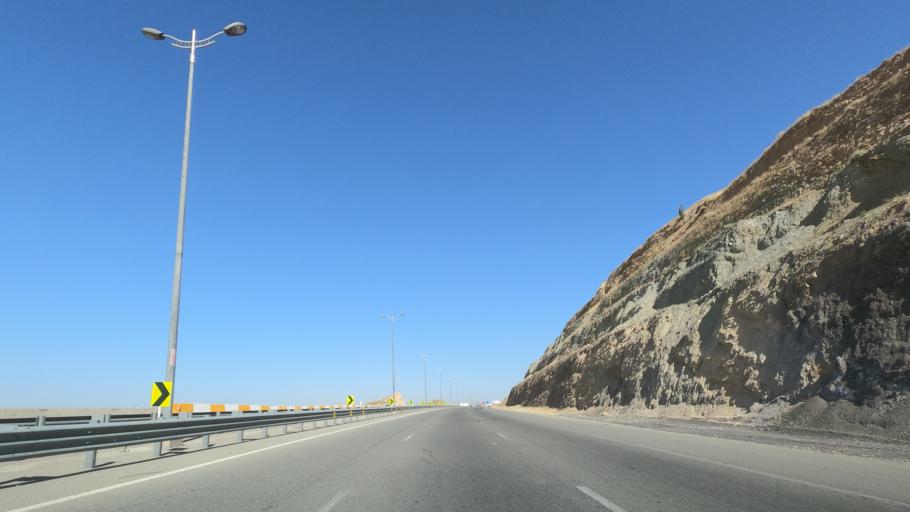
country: IR
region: Tehran
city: Shahr-e Qods
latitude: 35.7481
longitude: 51.0968
